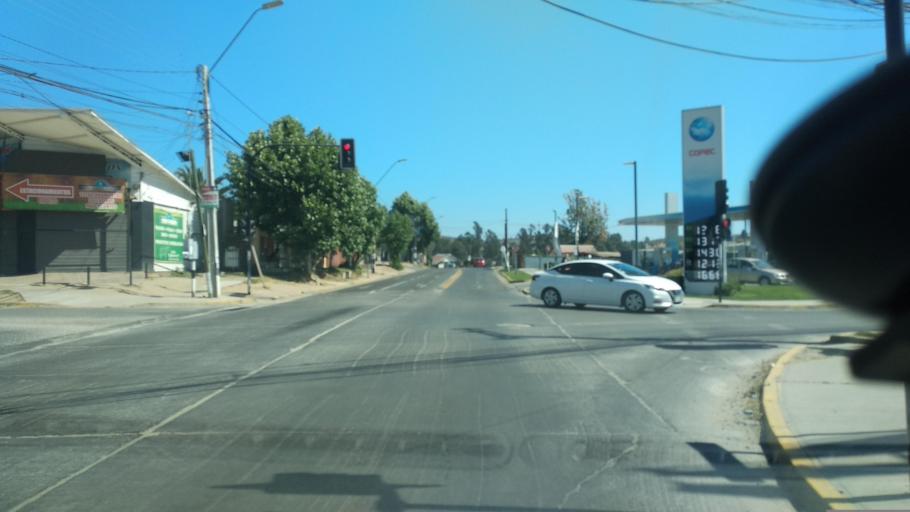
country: CL
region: Valparaiso
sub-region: Provincia de Marga Marga
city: Villa Alemana
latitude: -33.0586
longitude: -71.3725
